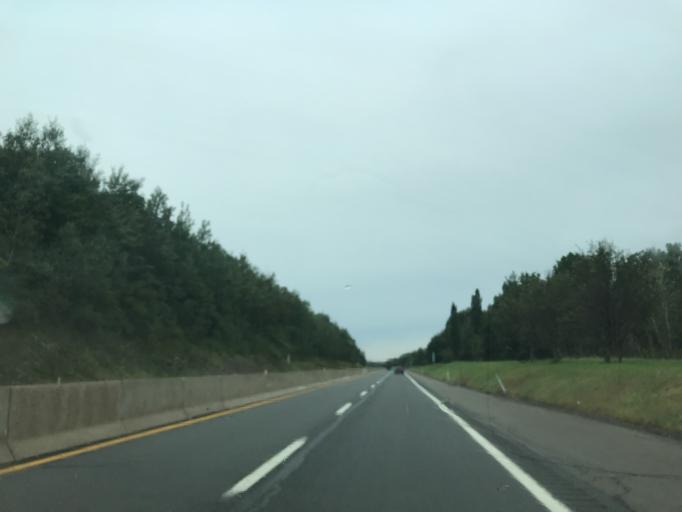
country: US
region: Pennsylvania
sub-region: Lackawanna County
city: Chinchilla
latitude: 41.4621
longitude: -75.6914
